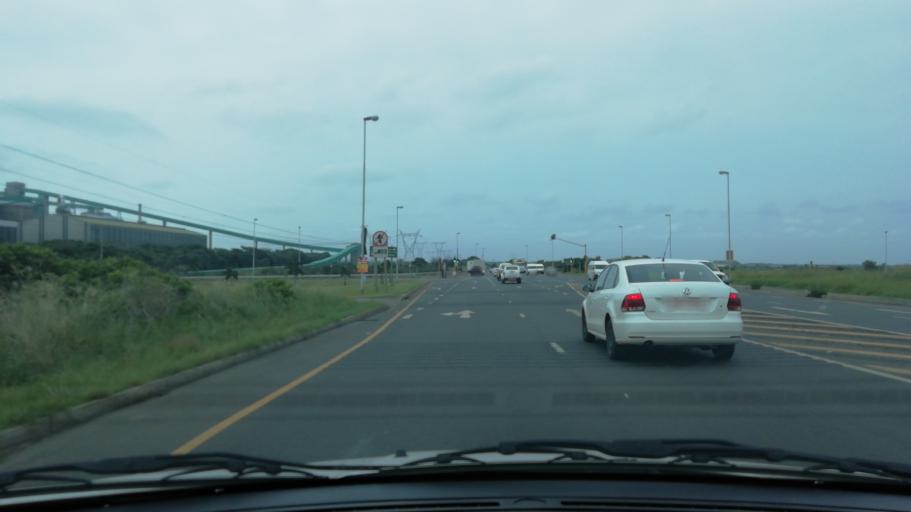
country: ZA
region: KwaZulu-Natal
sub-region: uThungulu District Municipality
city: Richards Bay
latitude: -28.7694
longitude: 32.0349
